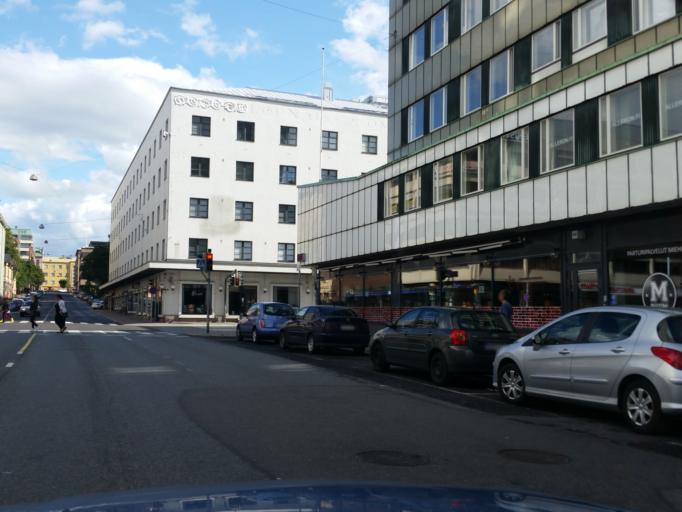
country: FI
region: Varsinais-Suomi
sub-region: Turku
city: Turku
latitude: 60.4512
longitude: 22.2573
